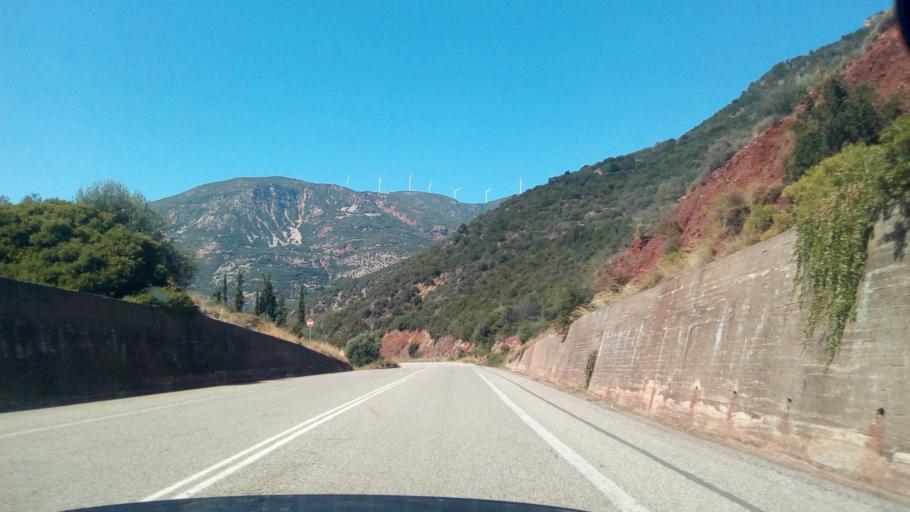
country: GR
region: West Greece
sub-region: Nomos Achaias
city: Selianitika
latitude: 38.3914
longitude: 22.0734
